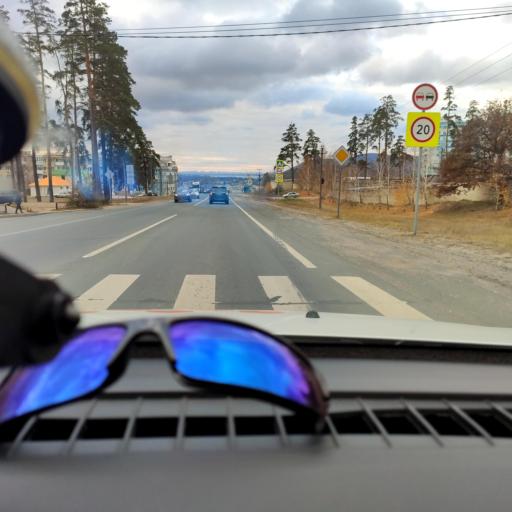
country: RU
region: Samara
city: Volzhskiy
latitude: 53.4383
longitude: 50.1243
